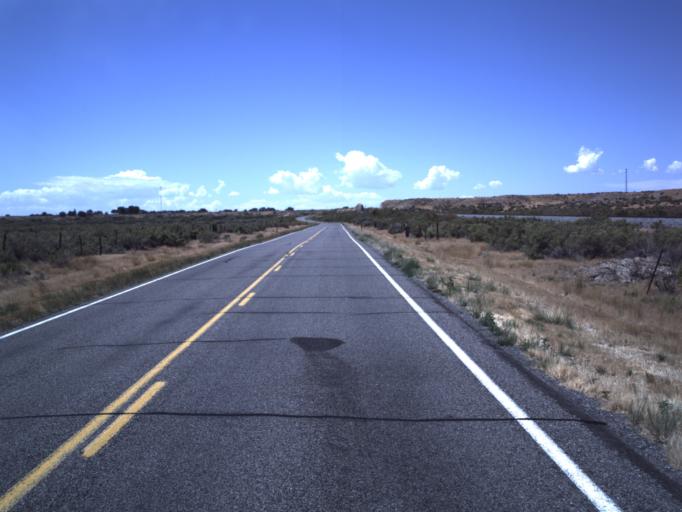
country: US
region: Utah
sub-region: Millard County
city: Delta
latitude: 39.5295
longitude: -112.3434
